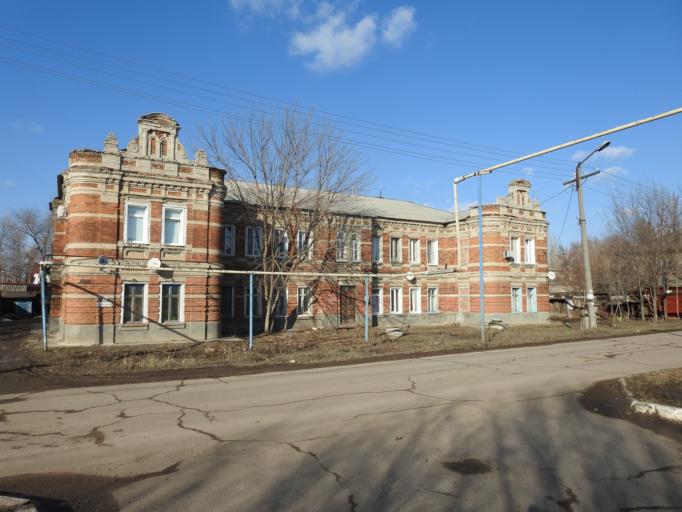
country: RU
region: Saratov
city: Yershov
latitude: 51.3498
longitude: 48.2798
